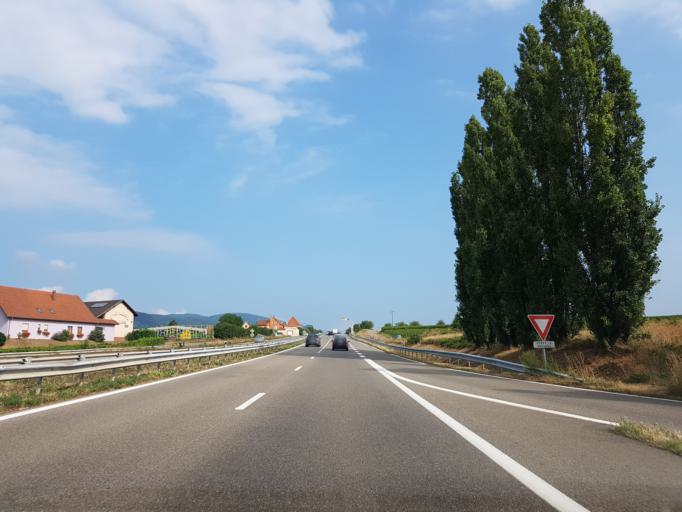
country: FR
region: Alsace
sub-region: Departement du Haut-Rhin
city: Pfaffenheim
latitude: 47.9786
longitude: 7.2946
